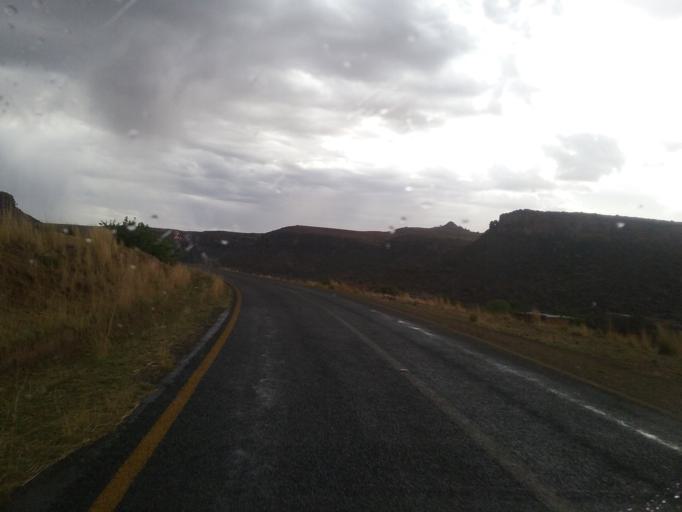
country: LS
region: Quthing
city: Quthing
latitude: -30.3113
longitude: 27.7390
